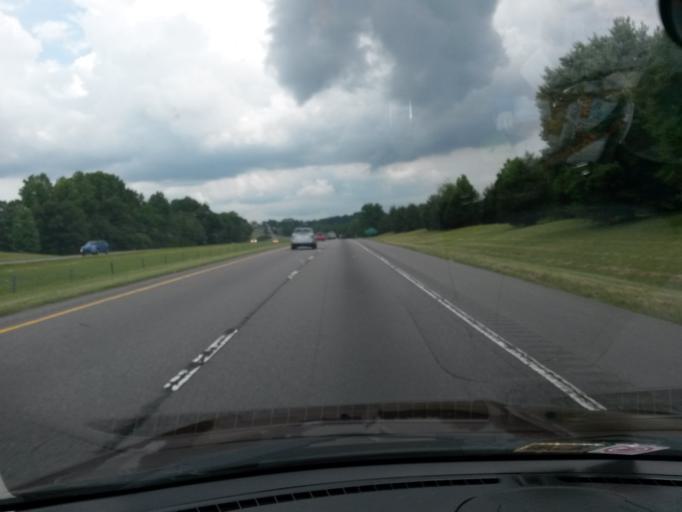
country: US
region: North Carolina
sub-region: Iredell County
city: Statesville
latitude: 35.9369
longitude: -80.8547
